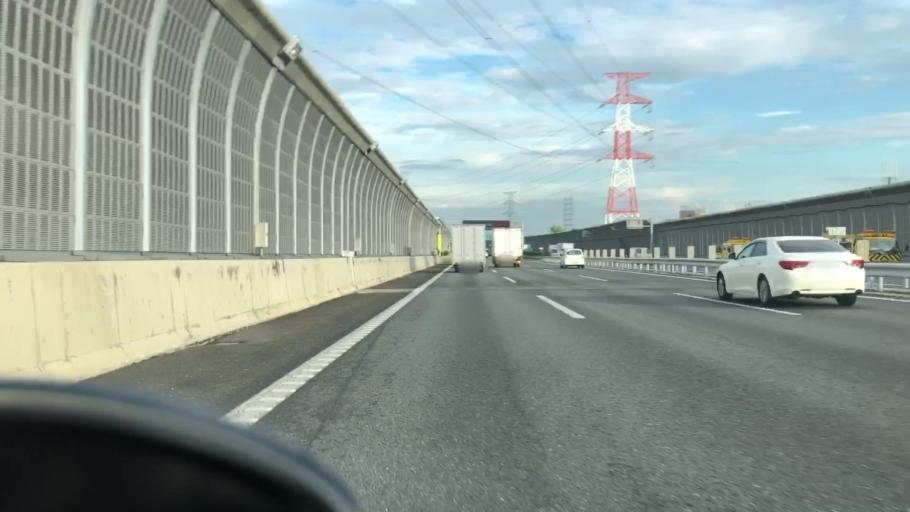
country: JP
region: Hyogo
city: Takarazuka
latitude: 34.8111
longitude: 135.3626
